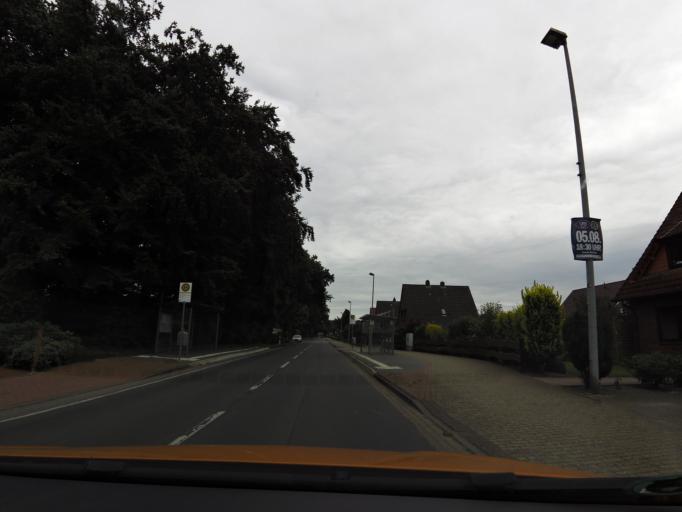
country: DE
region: Lower Saxony
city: Wiefelstede
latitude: 53.1892
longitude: 8.1560
